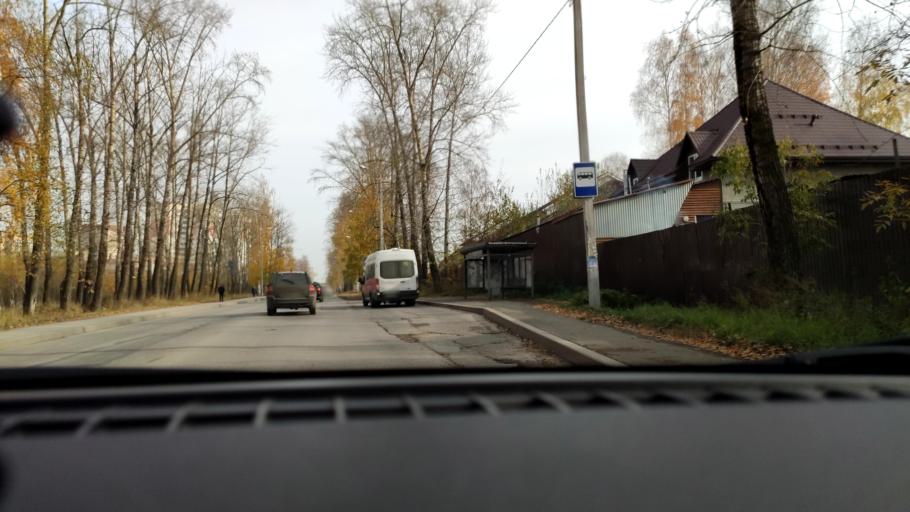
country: RU
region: Perm
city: Polazna
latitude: 58.1303
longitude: 56.3917
